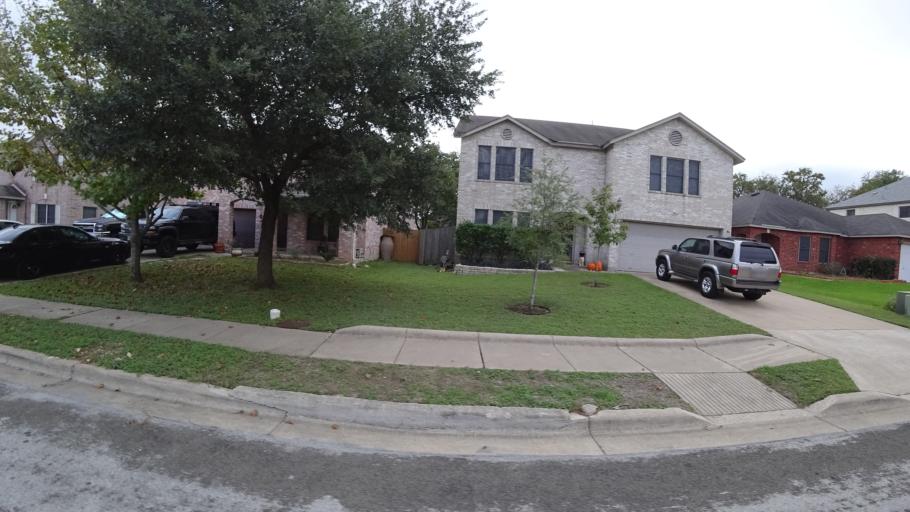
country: US
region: Texas
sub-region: Travis County
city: Manchaca
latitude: 30.1557
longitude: -97.8409
